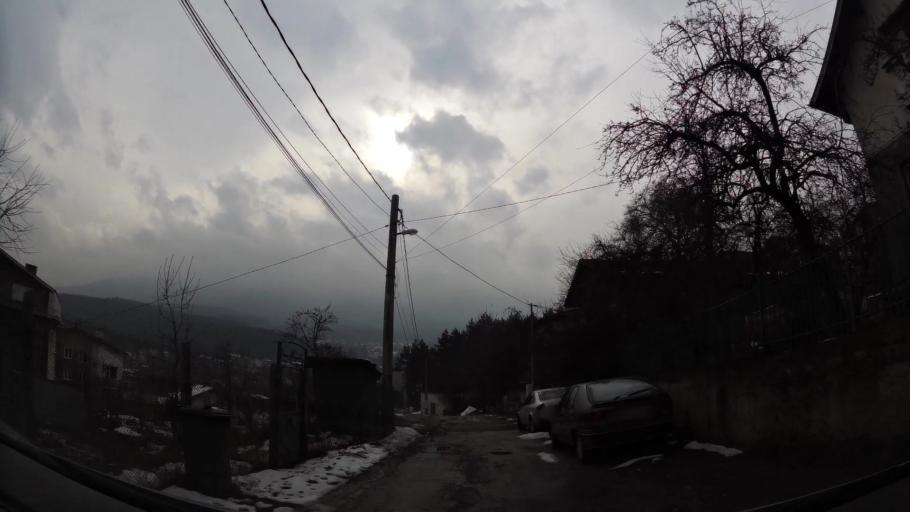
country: BG
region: Sofia-Capital
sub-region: Stolichna Obshtina
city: Sofia
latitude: 42.6603
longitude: 23.2380
